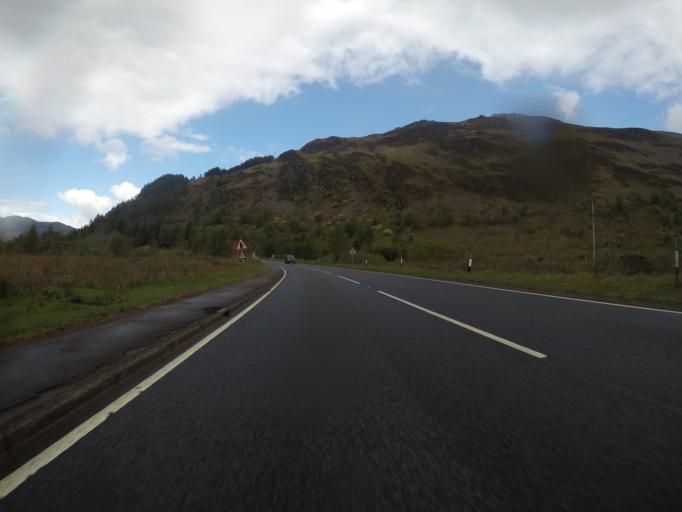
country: GB
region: Scotland
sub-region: Highland
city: Fort William
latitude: 57.2344
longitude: -5.4075
